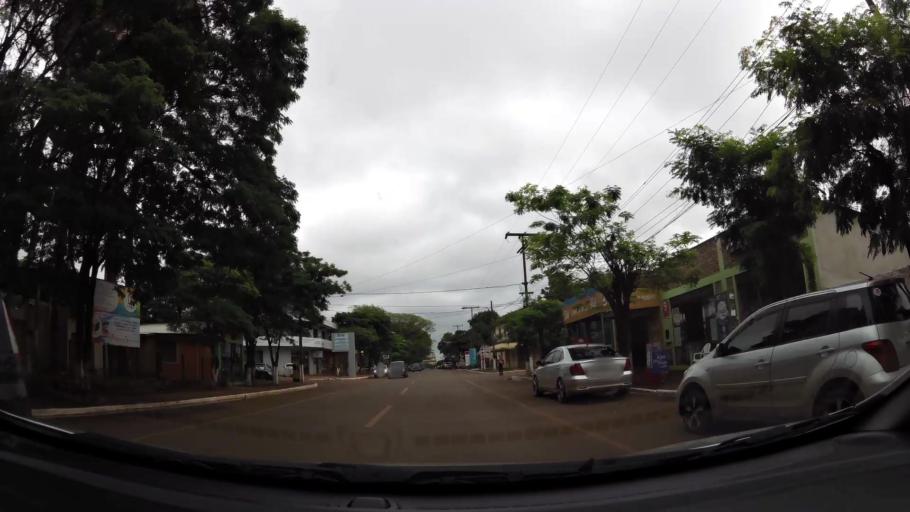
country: PY
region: Alto Parana
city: Ciudad del Este
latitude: -25.4857
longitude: -54.7601
